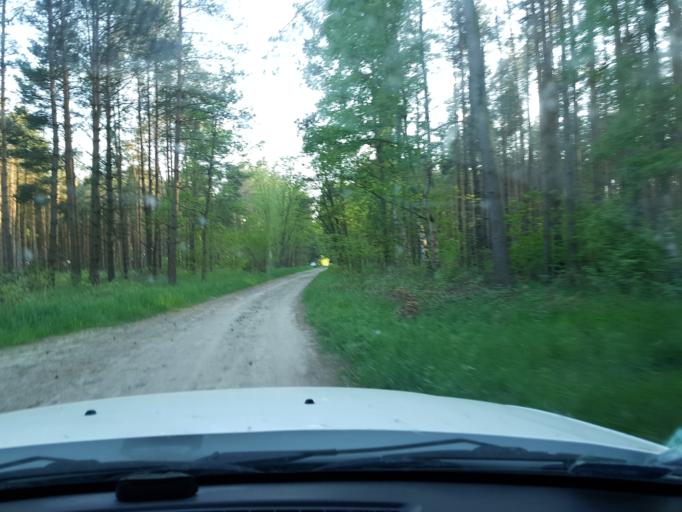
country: PL
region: West Pomeranian Voivodeship
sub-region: Powiat stargardzki
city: Kobylanka
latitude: 53.4113
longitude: 14.8984
